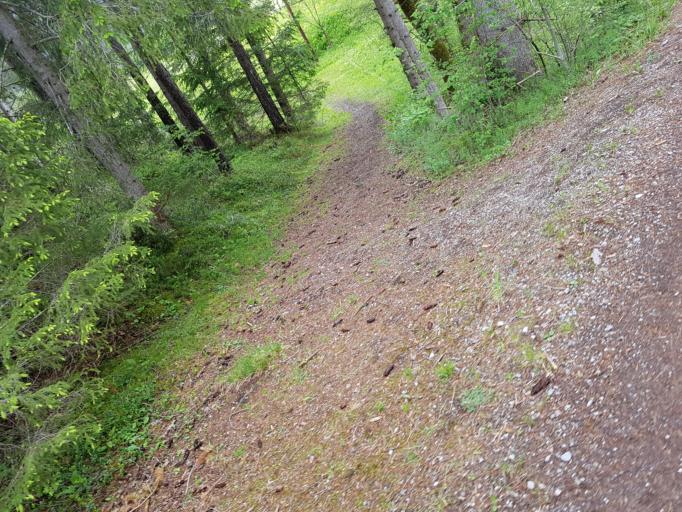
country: AT
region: Tyrol
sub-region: Politischer Bezirk Imst
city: Obsteig
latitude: 47.3053
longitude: 10.9435
